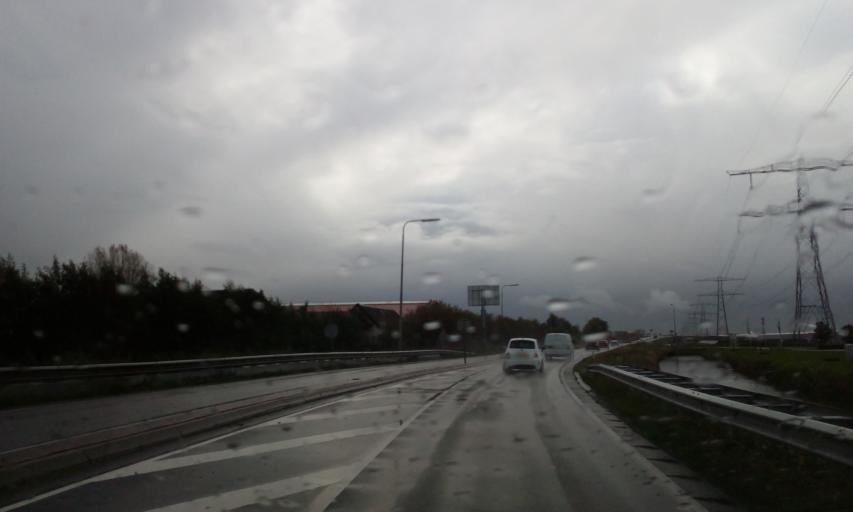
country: NL
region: South Holland
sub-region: Gemeente Westland
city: Kwintsheul
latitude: 52.0083
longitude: 4.2888
